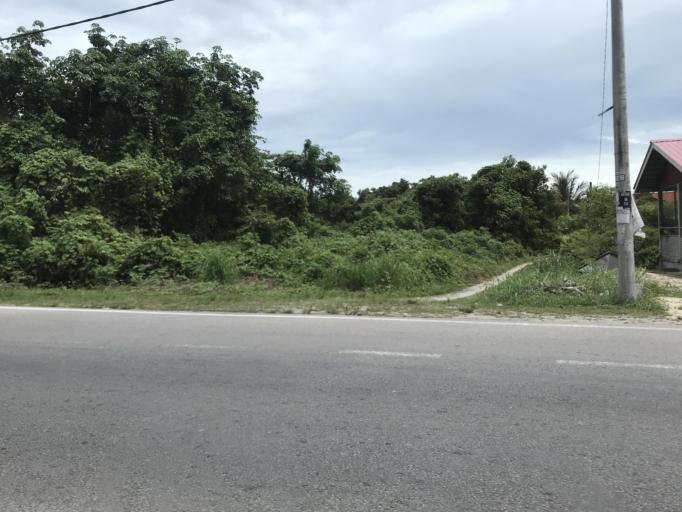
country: MY
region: Kelantan
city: Tumpat
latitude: 6.1674
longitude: 102.1909
